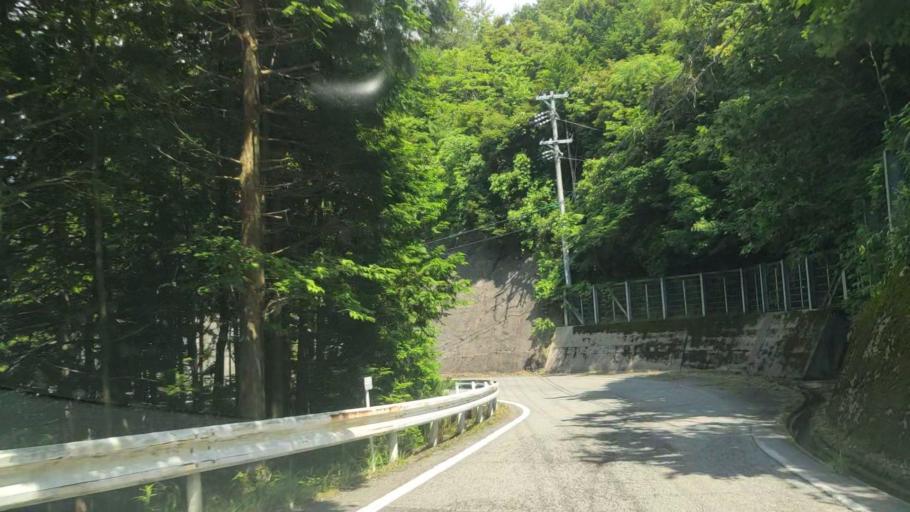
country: JP
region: Hyogo
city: Toyooka
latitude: 35.6386
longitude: 134.7694
